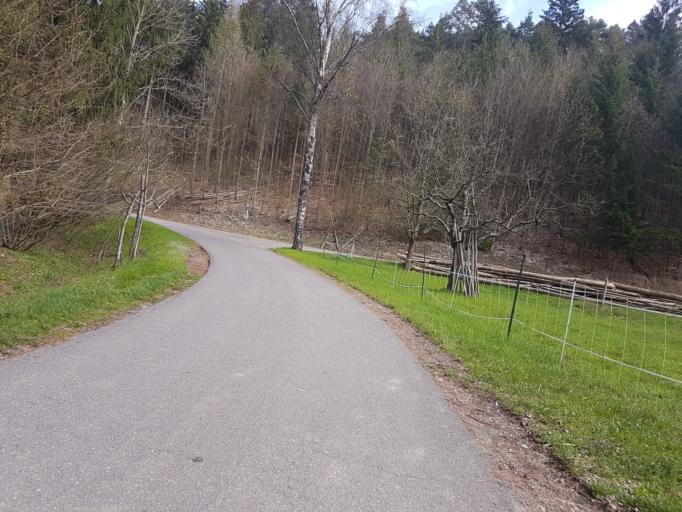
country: DE
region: Baden-Wuerttemberg
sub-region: Regierungsbezirk Stuttgart
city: Krautheim
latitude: 49.3550
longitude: 9.6130
